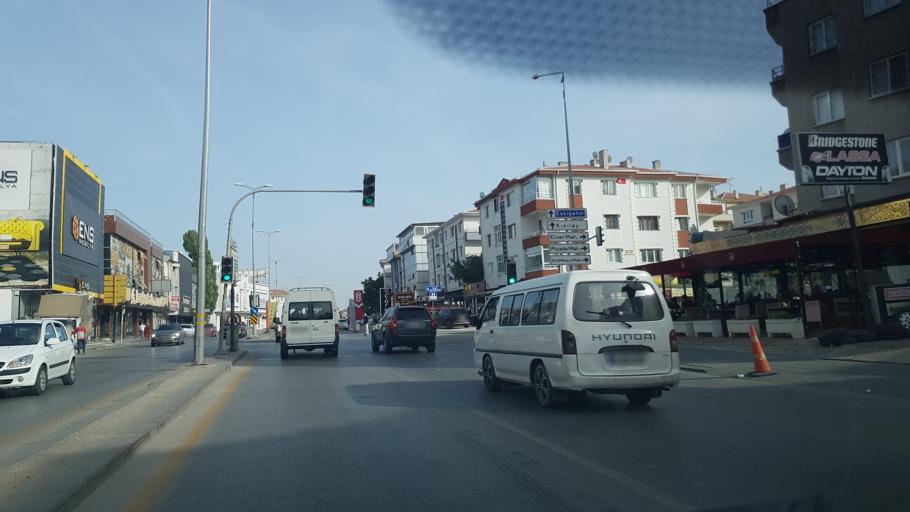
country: TR
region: Ankara
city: Etimesgut
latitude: 39.9545
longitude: 32.6330
